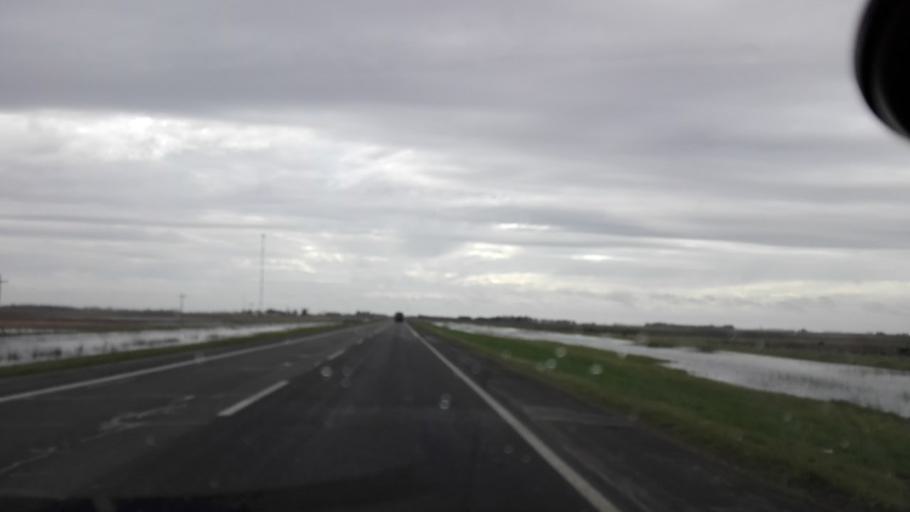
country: AR
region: Buenos Aires
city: San Miguel del Monte
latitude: -35.7353
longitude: -58.9145
